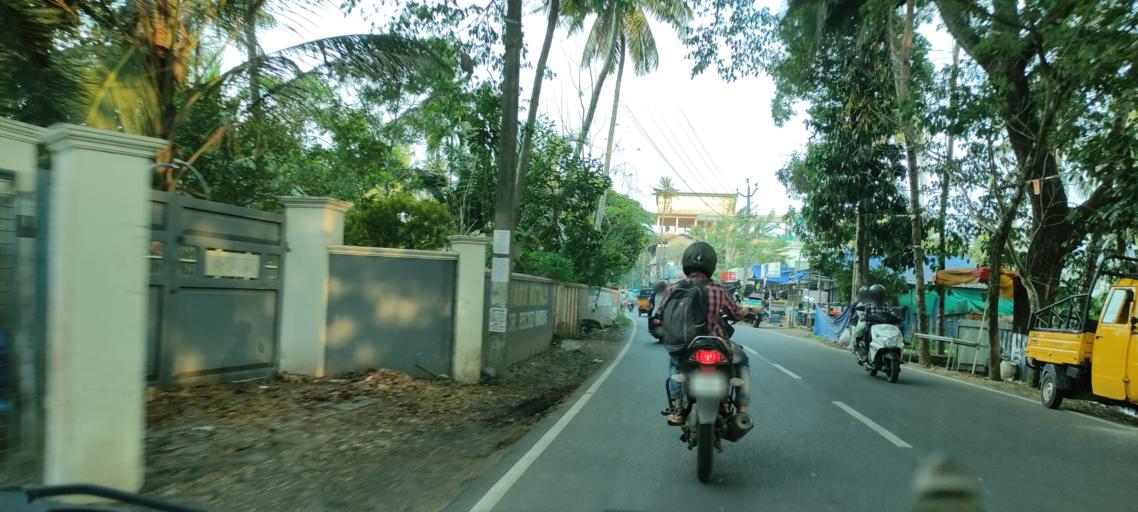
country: IN
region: Kerala
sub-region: Alappuzha
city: Arukutti
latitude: 9.8521
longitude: 76.3269
